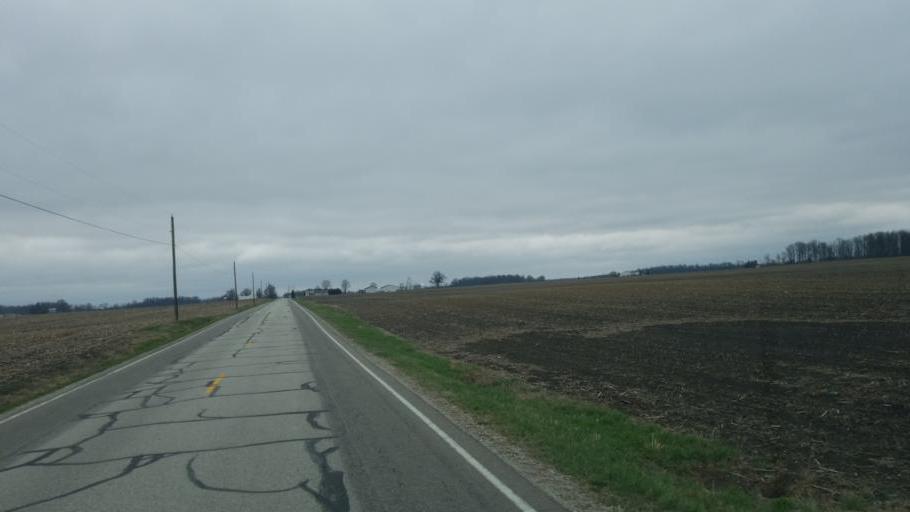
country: US
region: Ohio
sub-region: Crawford County
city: Bucyrus
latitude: 40.8368
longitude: -83.0164
